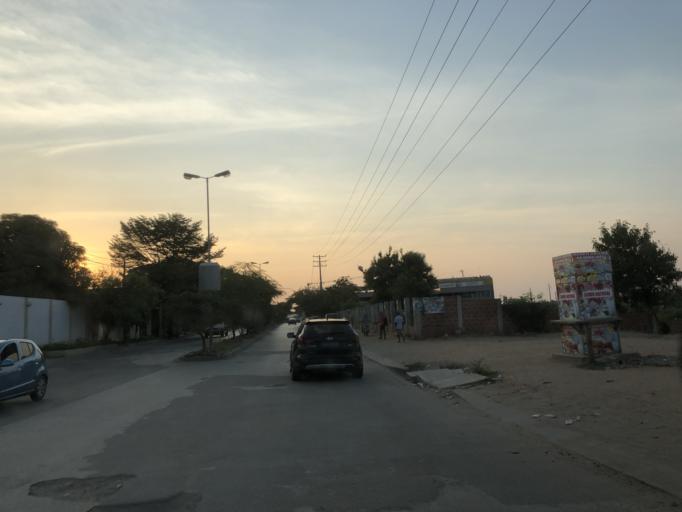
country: AO
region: Luanda
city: Luanda
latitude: -8.8991
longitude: 13.2314
